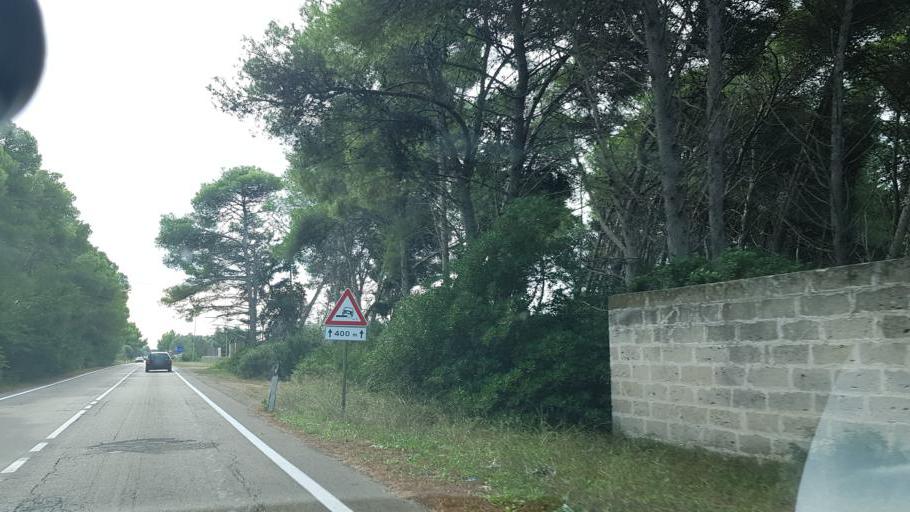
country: IT
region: Apulia
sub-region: Provincia di Lecce
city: Struda
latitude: 40.3662
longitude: 18.3118
